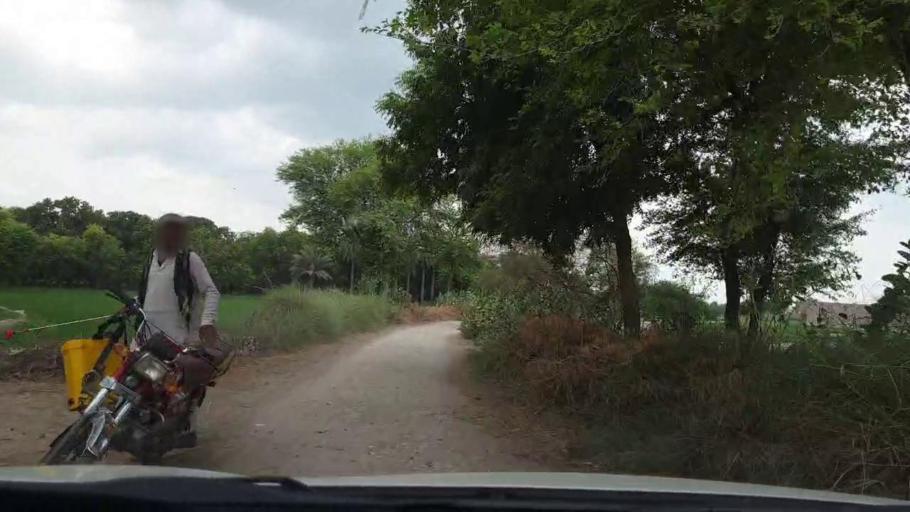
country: PK
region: Sindh
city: Dokri
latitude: 27.3247
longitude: 68.1026
